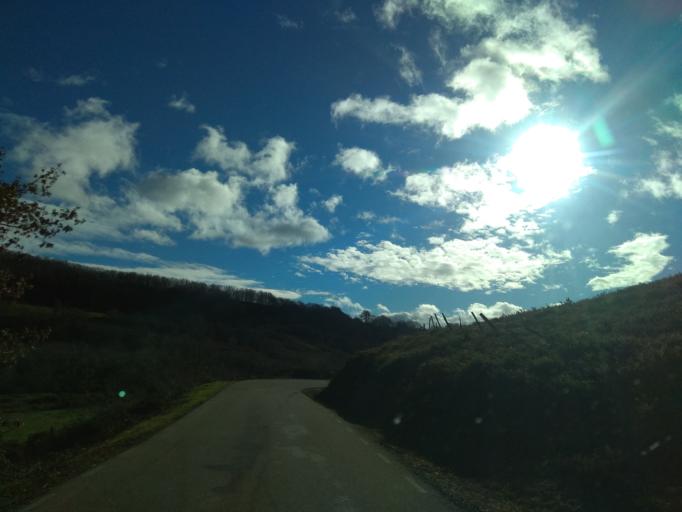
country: ES
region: Cantabria
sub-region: Provincia de Cantabria
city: San Martin de Elines
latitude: 42.9331
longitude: -3.8356
